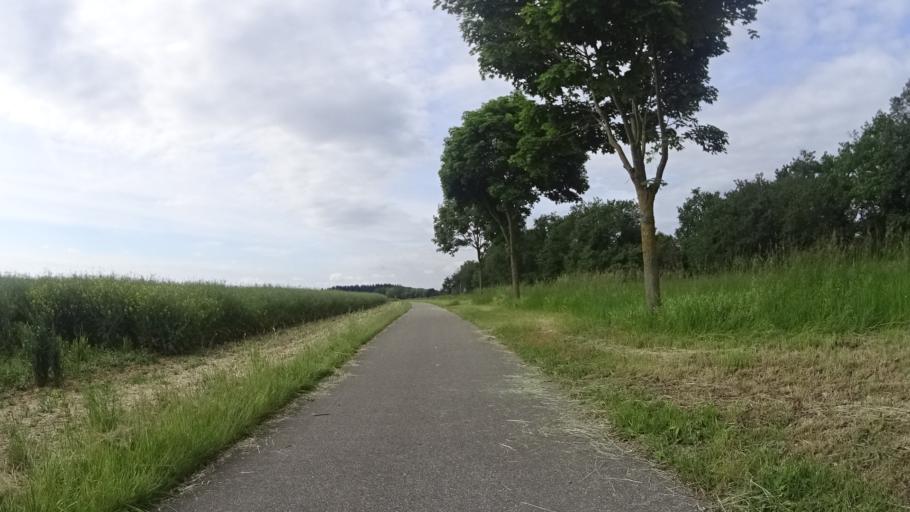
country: DE
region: Baden-Wuerttemberg
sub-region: Freiburg Region
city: Neuenburg am Rhein
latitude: 47.7936
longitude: 7.5557
